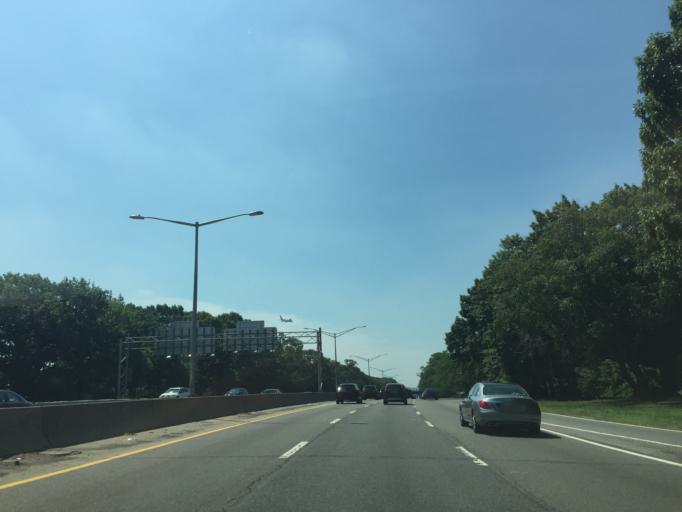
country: US
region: New York
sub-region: Nassau County
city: Bellerose Terrace
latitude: 40.7094
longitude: -73.7277
